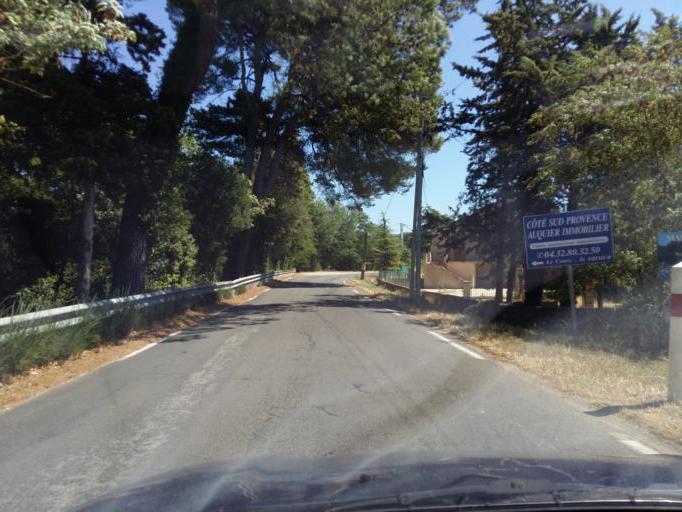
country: FR
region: Provence-Alpes-Cote d'Azur
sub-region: Departement du Vaucluse
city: Saint-Didier
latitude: 44.0158
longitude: 5.1018
